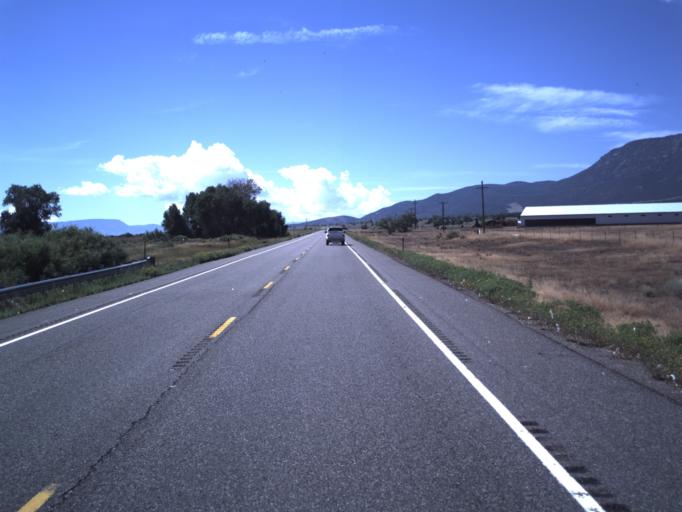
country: US
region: Utah
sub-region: Piute County
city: Junction
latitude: 38.4073
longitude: -112.2313
